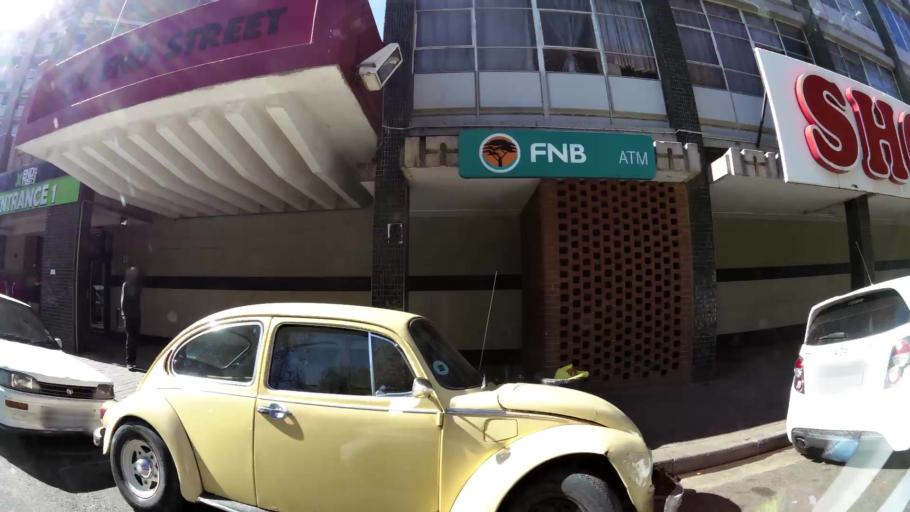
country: ZA
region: Gauteng
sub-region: City of Johannesburg Metropolitan Municipality
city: Johannesburg
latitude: -26.1981
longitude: 28.0529
